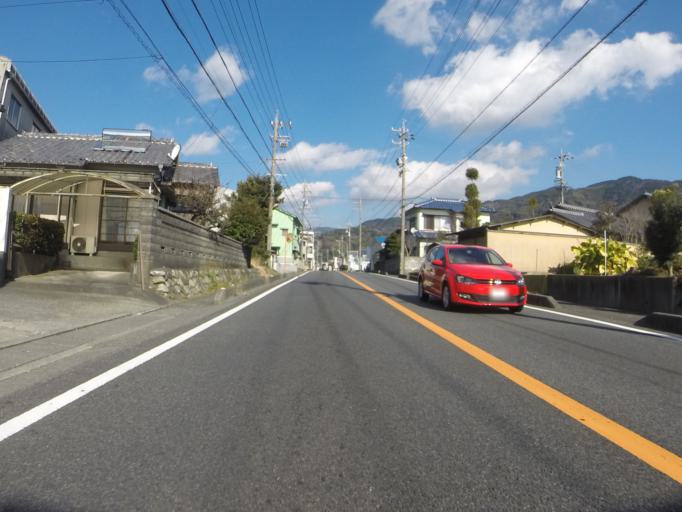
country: JP
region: Shizuoka
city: Shizuoka-shi
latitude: 35.0728
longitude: 138.5210
